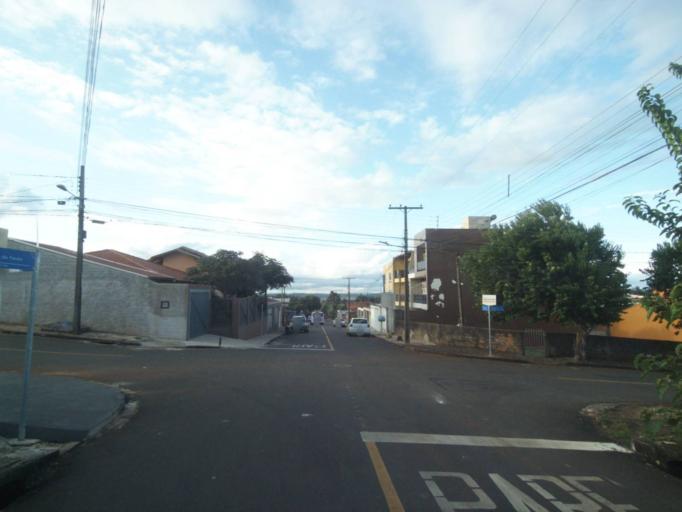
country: BR
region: Parana
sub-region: Telemaco Borba
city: Telemaco Borba
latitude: -24.3278
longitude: -50.6412
